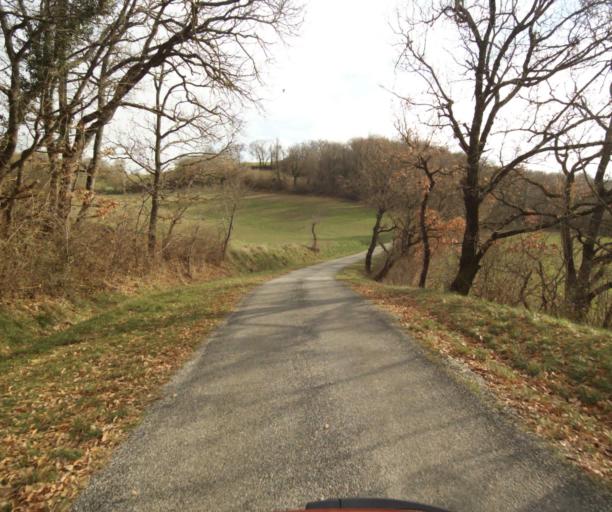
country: FR
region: Languedoc-Roussillon
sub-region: Departement de l'Aude
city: Belpech
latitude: 43.1679
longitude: 1.7378
